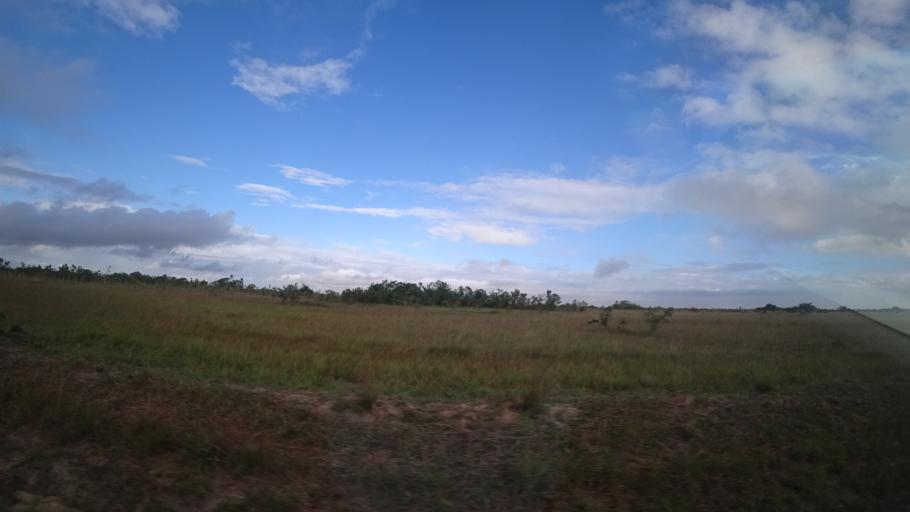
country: MZ
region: Sofala
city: Beira
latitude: -19.6777
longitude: 35.0595
